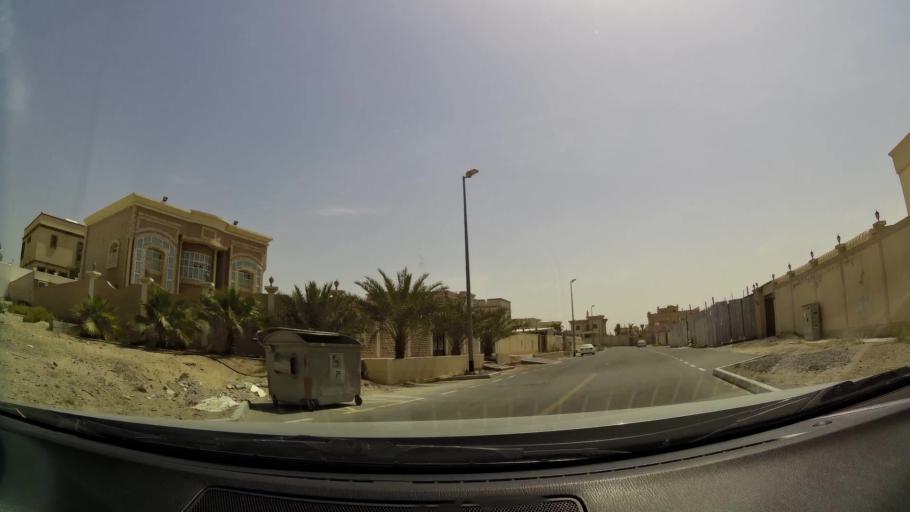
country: AE
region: Ash Shariqah
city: Sharjah
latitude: 25.1869
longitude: 55.4185
